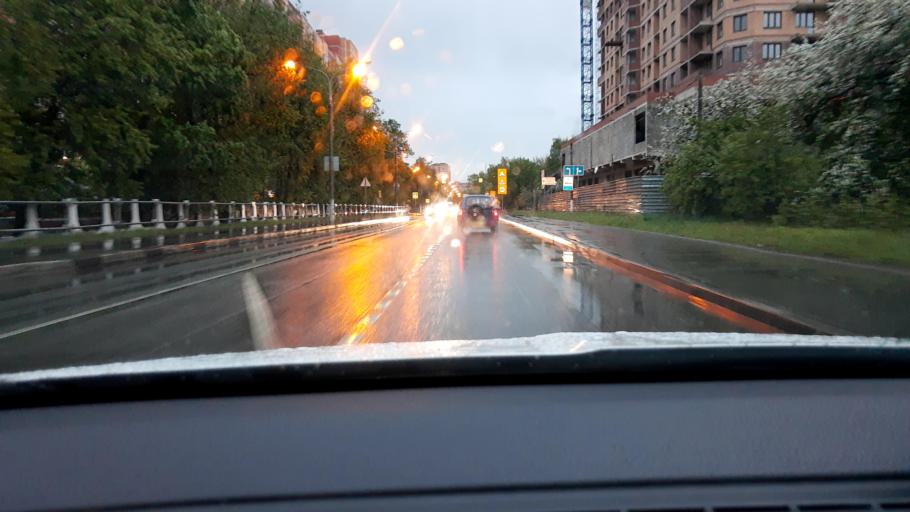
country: RU
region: Moskovskaya
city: Shchelkovo
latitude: 55.9193
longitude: 37.9814
